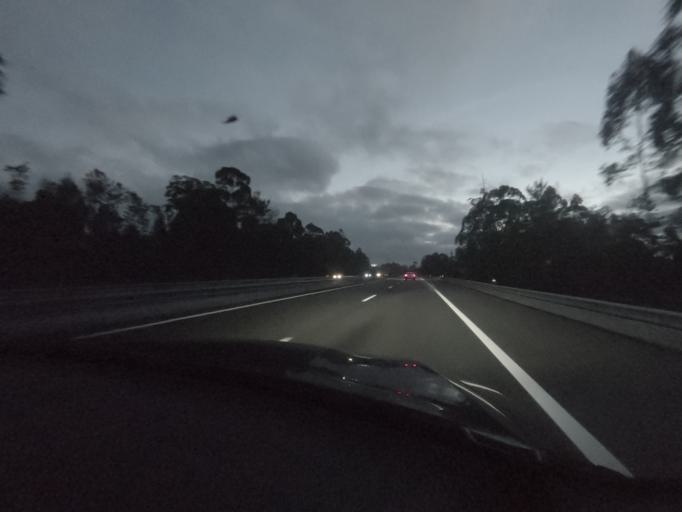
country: PT
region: Leiria
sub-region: Pombal
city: Pombal
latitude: 39.8824
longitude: -8.6960
